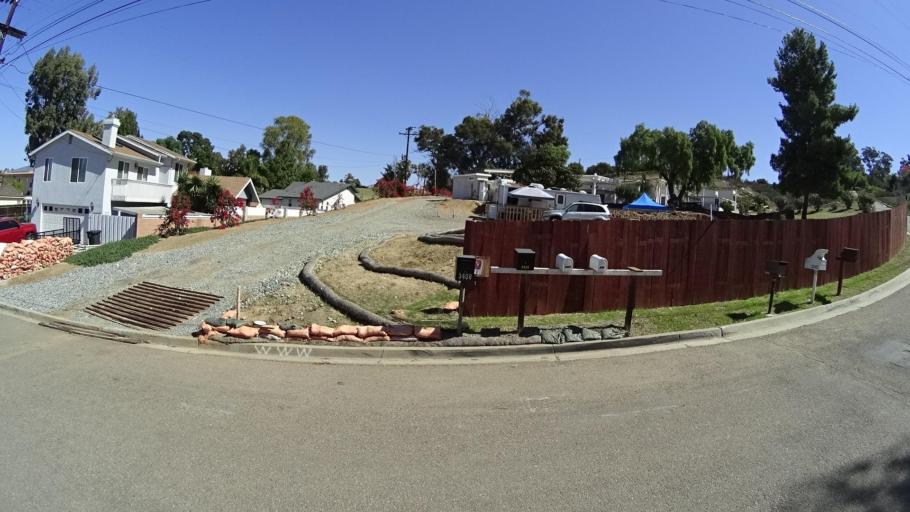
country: US
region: California
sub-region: San Diego County
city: Bonita
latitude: 32.6504
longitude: -117.0482
